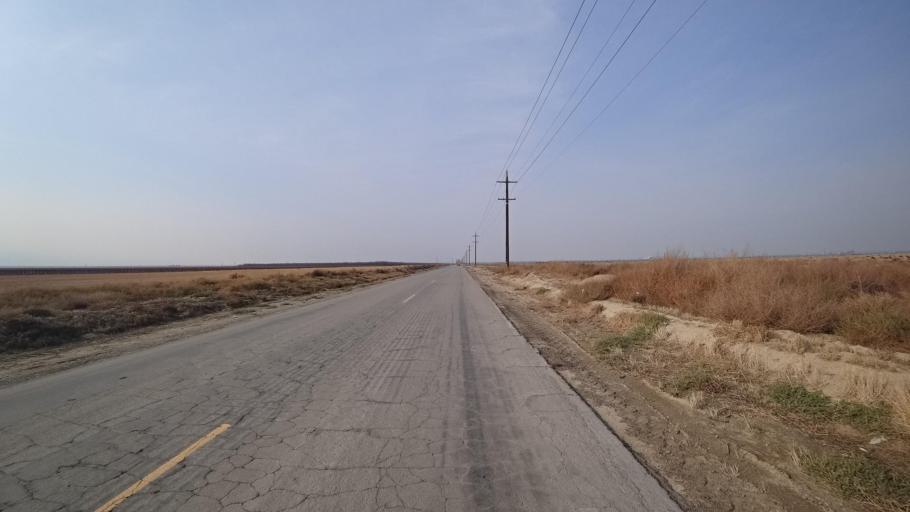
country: US
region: California
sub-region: Kern County
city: Greenfield
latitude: 35.0948
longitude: -119.0768
